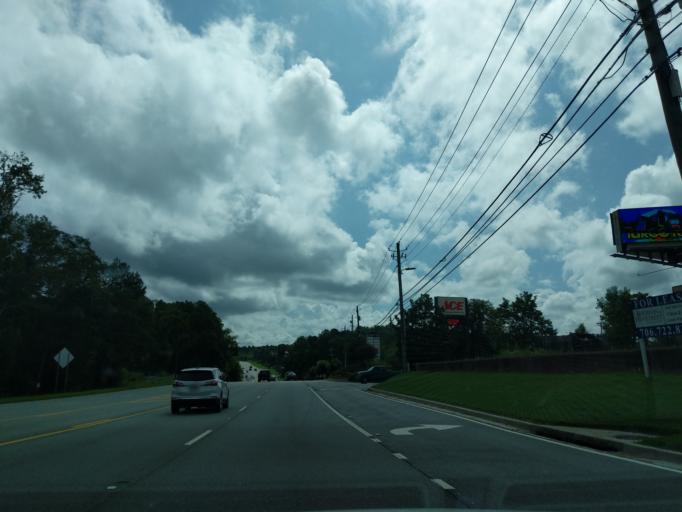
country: US
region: Georgia
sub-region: Columbia County
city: Evans
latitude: 33.5478
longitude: -82.1494
